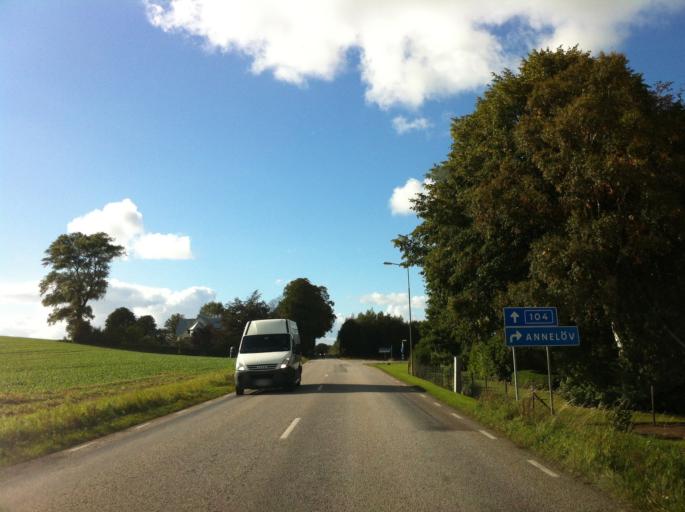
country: SE
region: Skane
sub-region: Kavlinge Kommun
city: Loddekopinge
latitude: 55.8127
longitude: 13.0531
